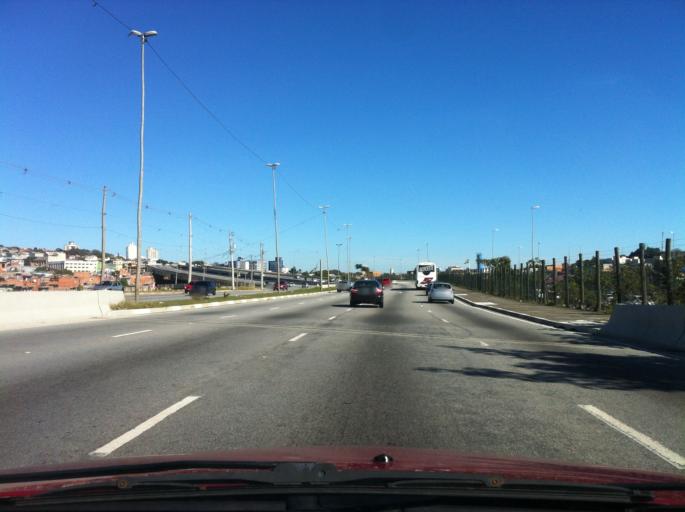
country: BR
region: Sao Paulo
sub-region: Guarulhos
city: Guarulhos
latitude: -23.4874
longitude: -46.4531
